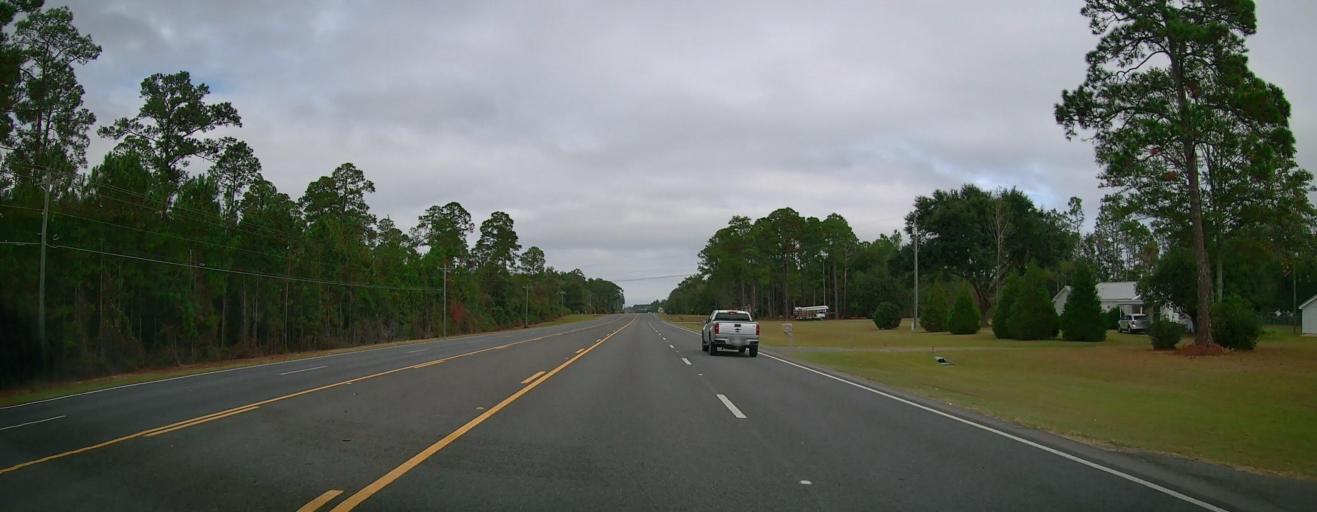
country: US
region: Georgia
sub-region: Colquitt County
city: Moultrie
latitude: 31.0960
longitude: -83.8017
